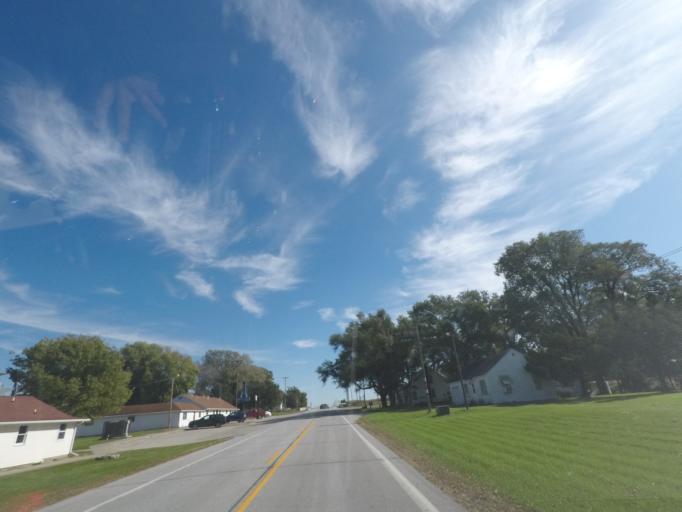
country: US
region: Iowa
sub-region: Story County
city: Nevada
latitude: 42.0225
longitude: -93.3110
